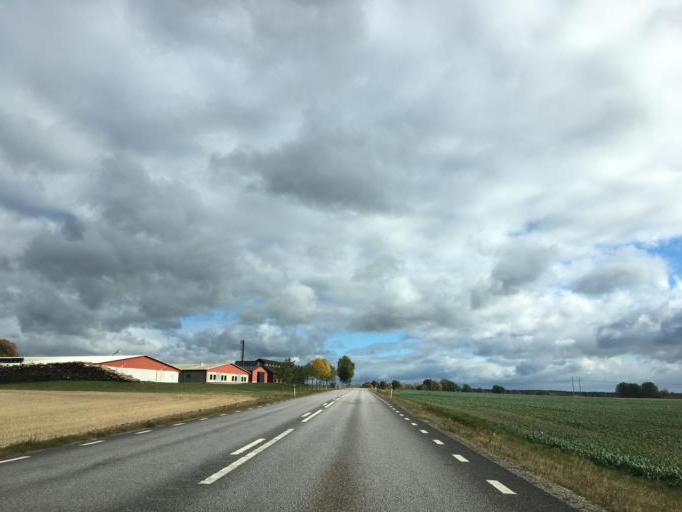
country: SE
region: Soedermanland
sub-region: Katrineholms Kommun
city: Katrineholm
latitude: 58.9679
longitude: 16.3456
